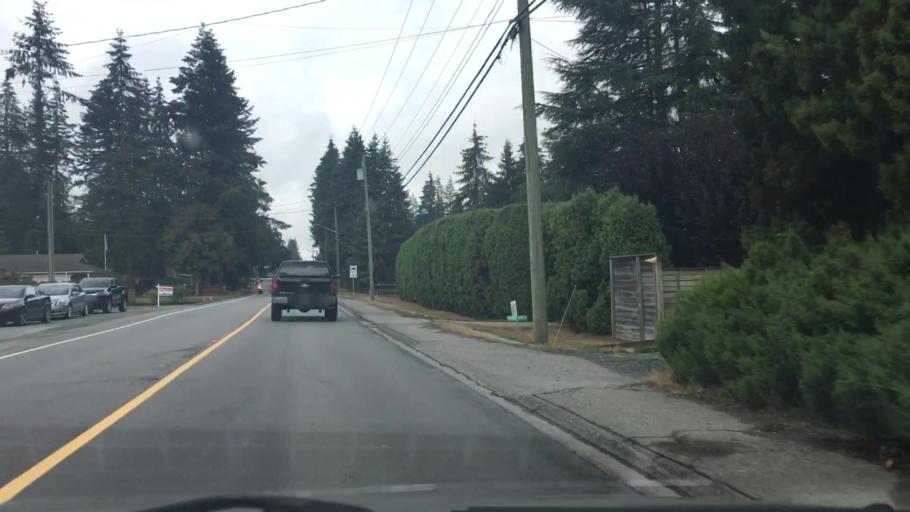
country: CA
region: British Columbia
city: Langley
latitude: 49.1040
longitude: -122.5328
